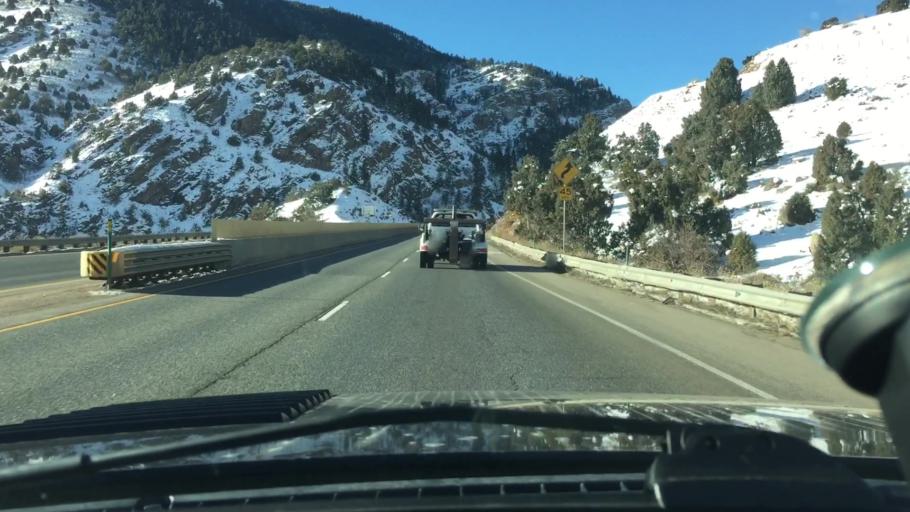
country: US
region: Colorado
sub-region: Jefferson County
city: Indian Hills
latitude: 39.6225
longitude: -105.1950
